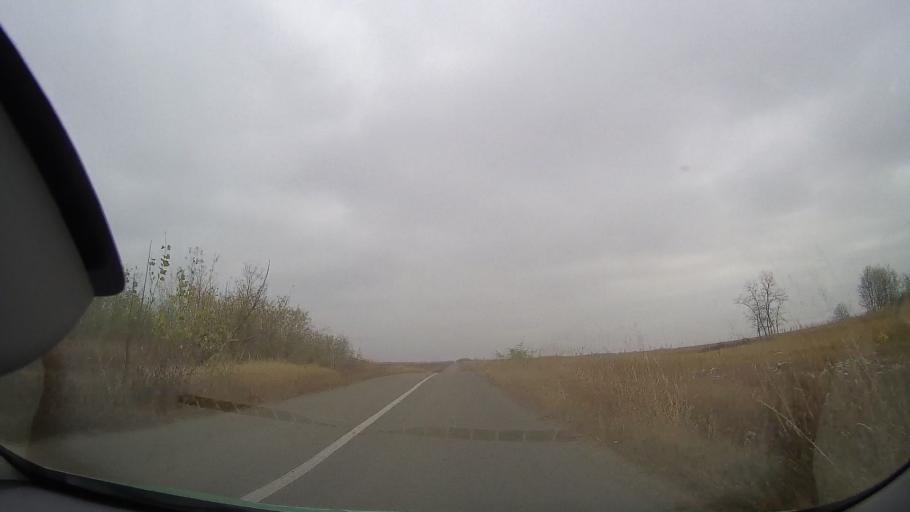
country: RO
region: Buzau
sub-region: Comuna Scutelnici
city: Scutelnici
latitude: 44.8739
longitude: 26.8844
